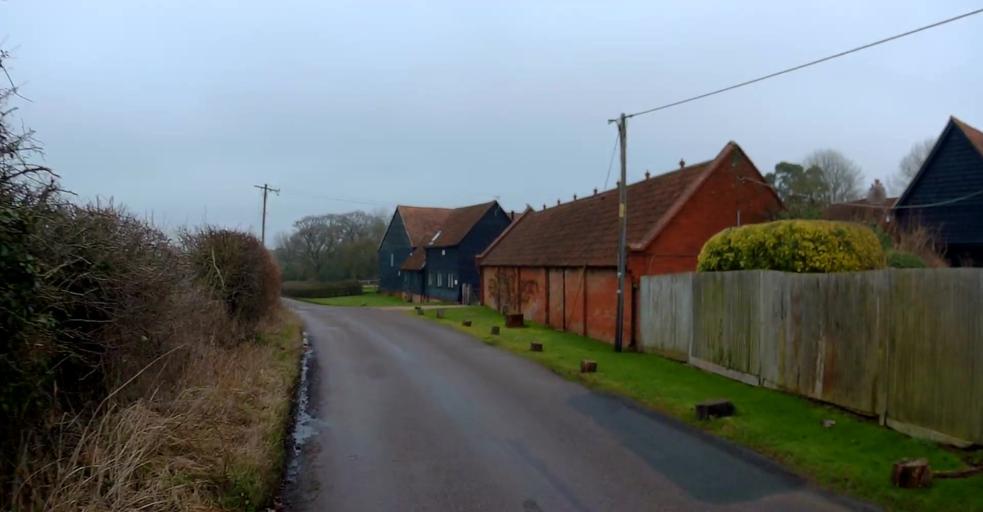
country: GB
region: England
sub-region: Hampshire
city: Hook
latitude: 51.3068
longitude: -0.9584
